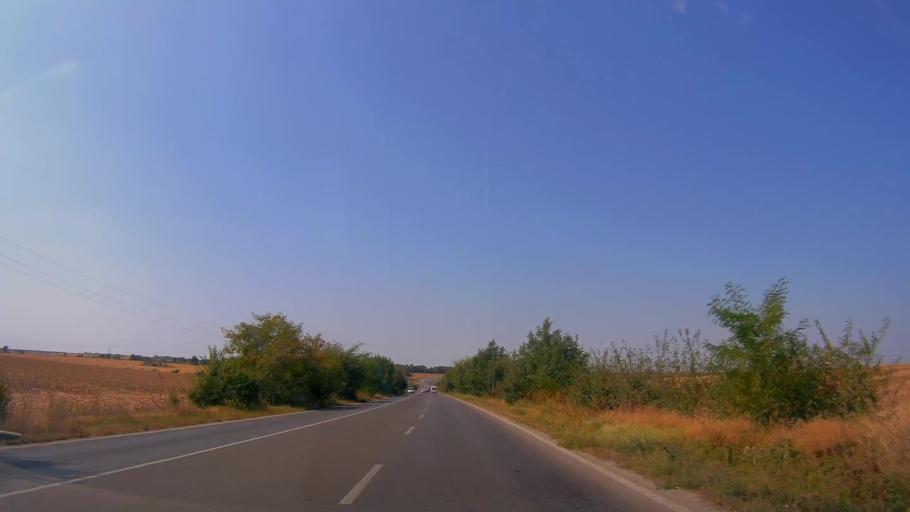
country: BG
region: Ruse
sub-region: Obshtina Vetovo
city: Senovo
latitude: 43.5662
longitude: 26.3308
